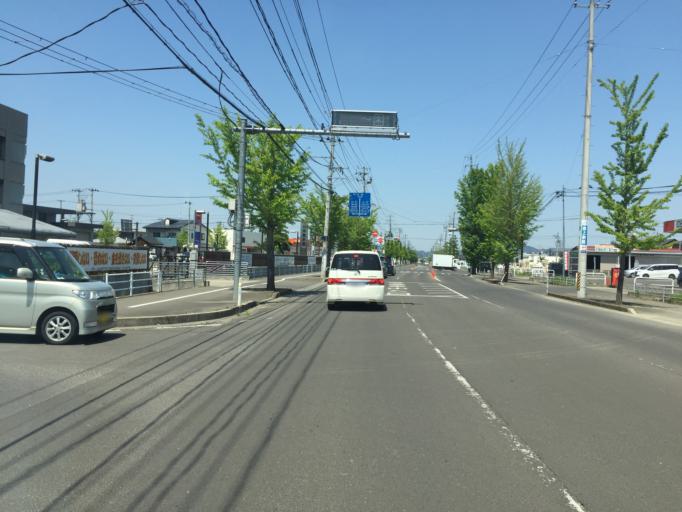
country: JP
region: Miyagi
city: Kakuda
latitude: 37.9765
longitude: 140.7883
